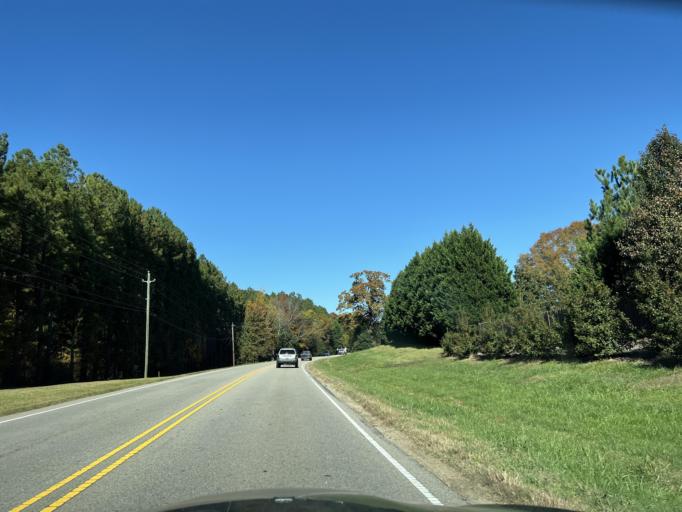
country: US
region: North Carolina
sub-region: Wake County
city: Garner
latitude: 35.7048
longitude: -78.6891
